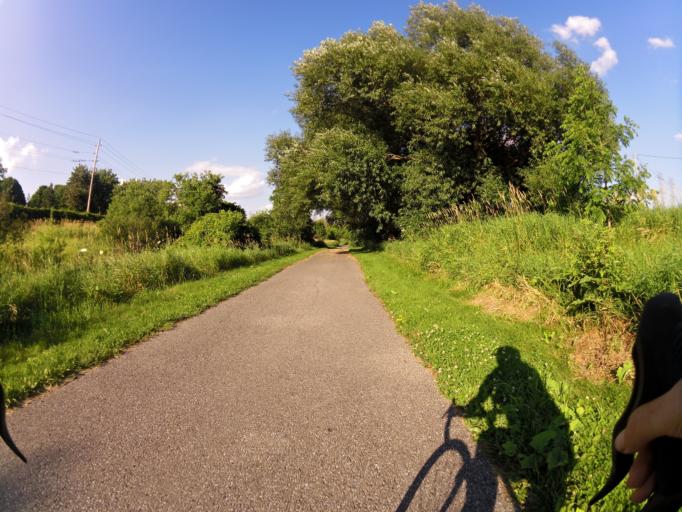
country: CA
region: Ontario
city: Ottawa
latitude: 45.3433
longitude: -75.7234
